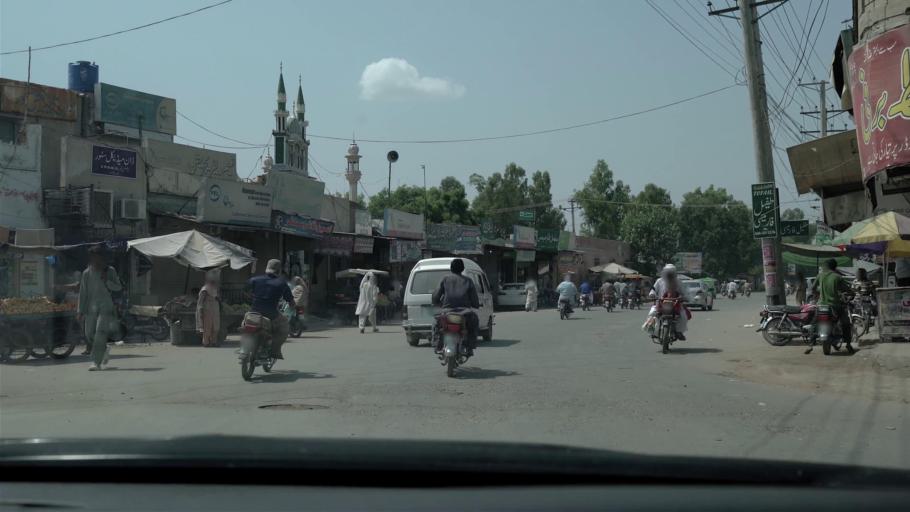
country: PK
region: Punjab
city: Gojra
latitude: 31.1523
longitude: 72.6762
